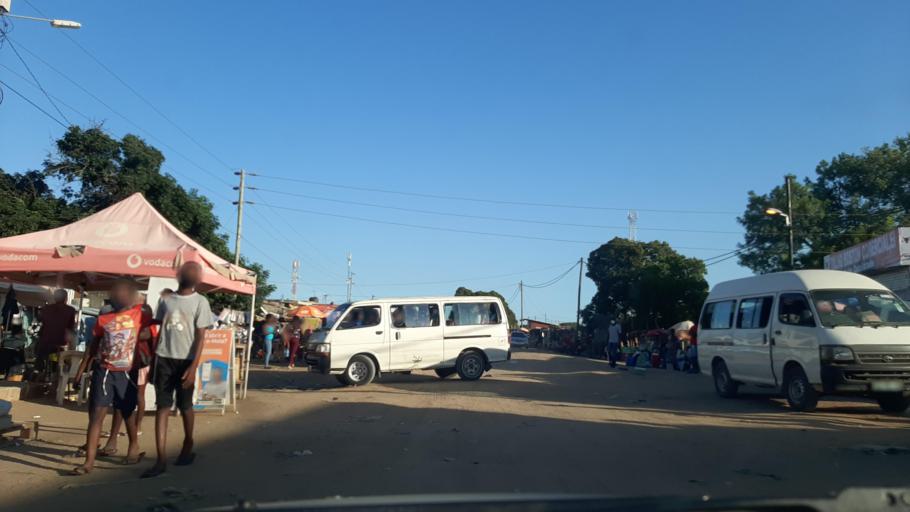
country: MZ
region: Maputo City
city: Maputo
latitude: -25.7372
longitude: 32.5389
